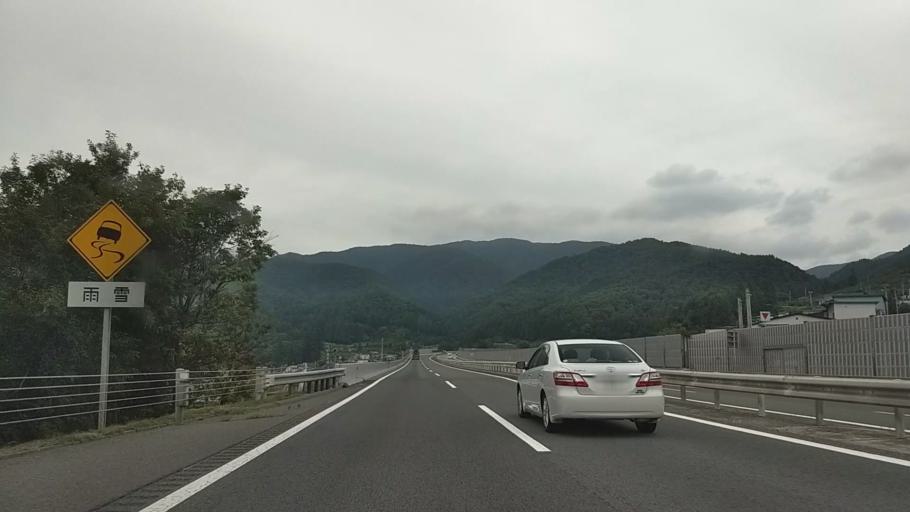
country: JP
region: Nagano
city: Nagano-shi
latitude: 36.5221
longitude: 138.0779
